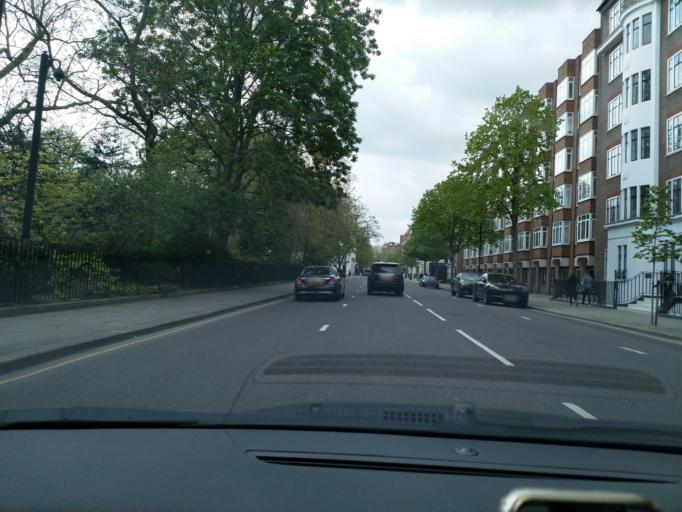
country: GB
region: England
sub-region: Greater London
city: Chelsea
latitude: 51.4958
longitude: -0.1585
